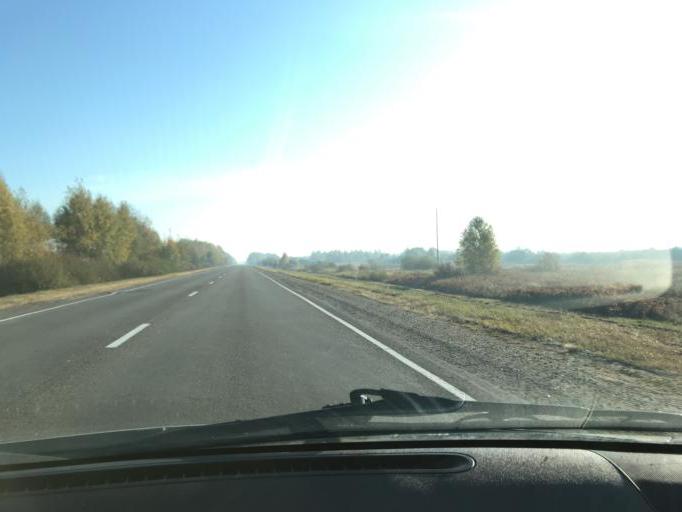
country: BY
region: Brest
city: Horad Luninyets
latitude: 52.3095
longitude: 26.5258
